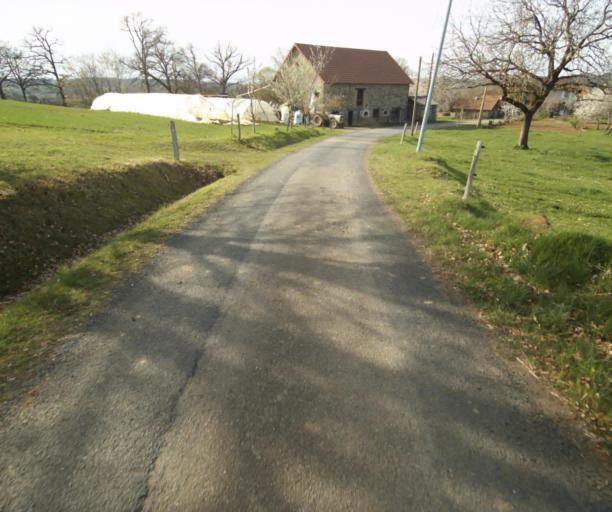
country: FR
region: Limousin
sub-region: Departement de la Correze
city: Naves
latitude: 45.3035
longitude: 1.7320
